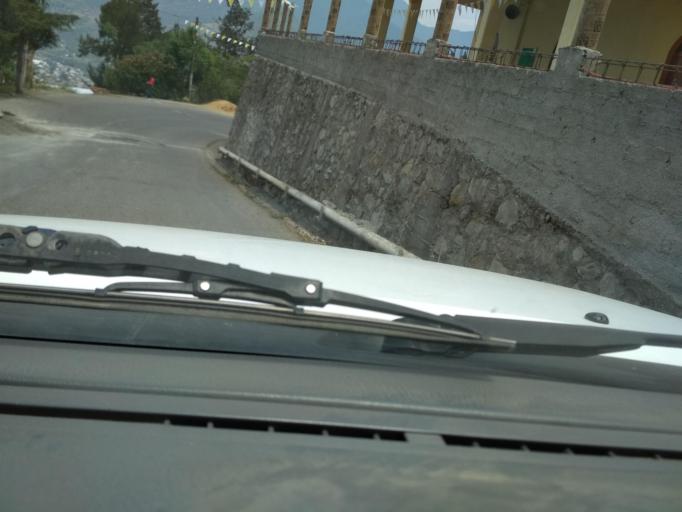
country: MX
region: Veracruz
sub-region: Camerino Z. Mendoza
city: La Cuesta
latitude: 18.7937
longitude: -97.1699
